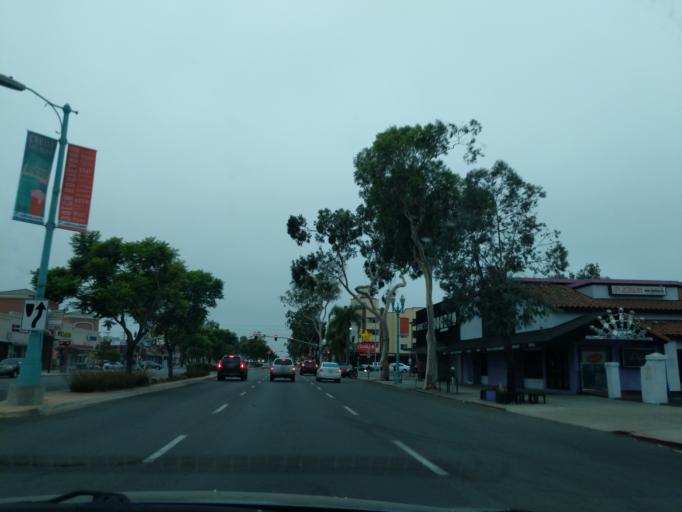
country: US
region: California
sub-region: San Diego County
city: San Diego
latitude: 32.7554
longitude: -117.1290
